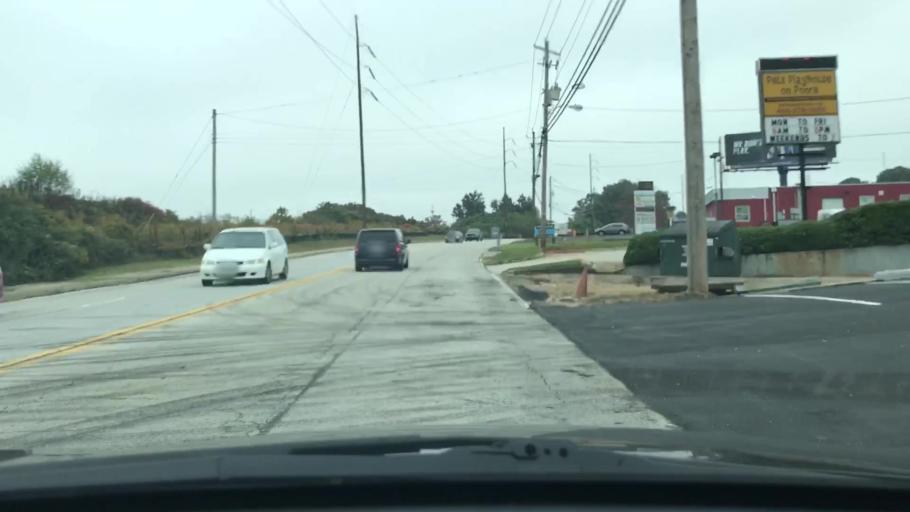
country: US
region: Georgia
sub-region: DeKalb County
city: Scottdale
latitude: 33.7831
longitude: -84.2728
